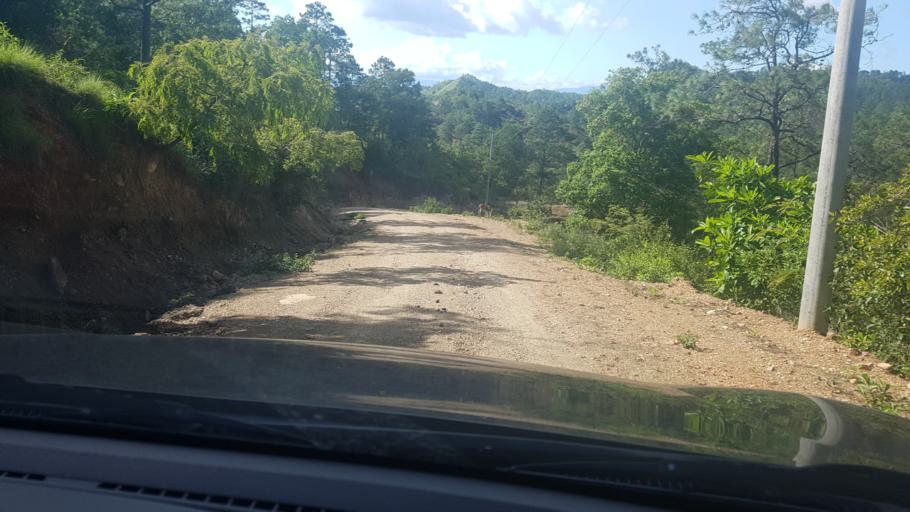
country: HN
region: Choluteca
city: Duyure
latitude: 13.6467
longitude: -86.6542
